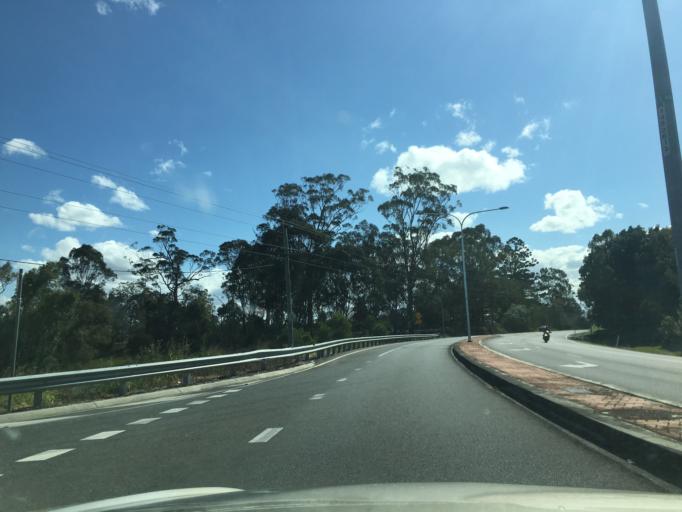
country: AU
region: Queensland
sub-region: Logan
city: Waterford West
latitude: -27.7091
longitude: 153.1449
